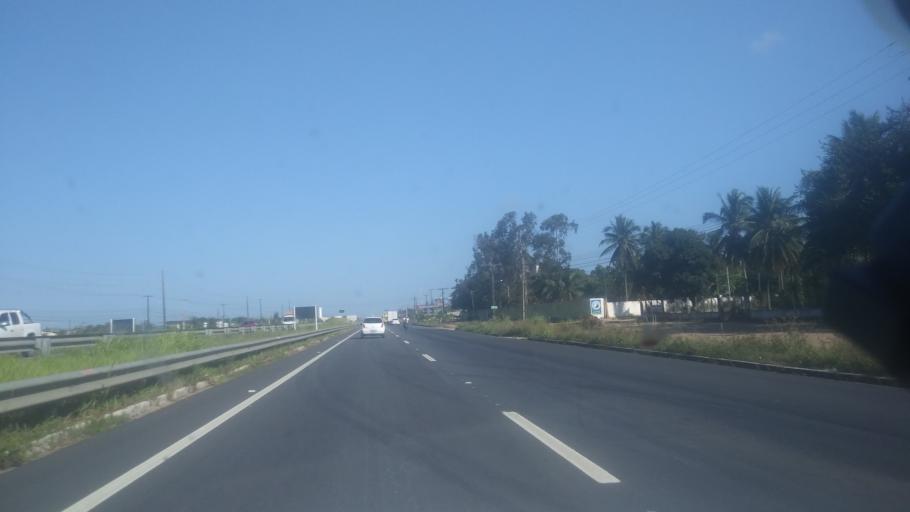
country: BR
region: Rio Grande do Norte
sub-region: Parnamirim
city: Parnamirim
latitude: -5.8841
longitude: -35.2834
